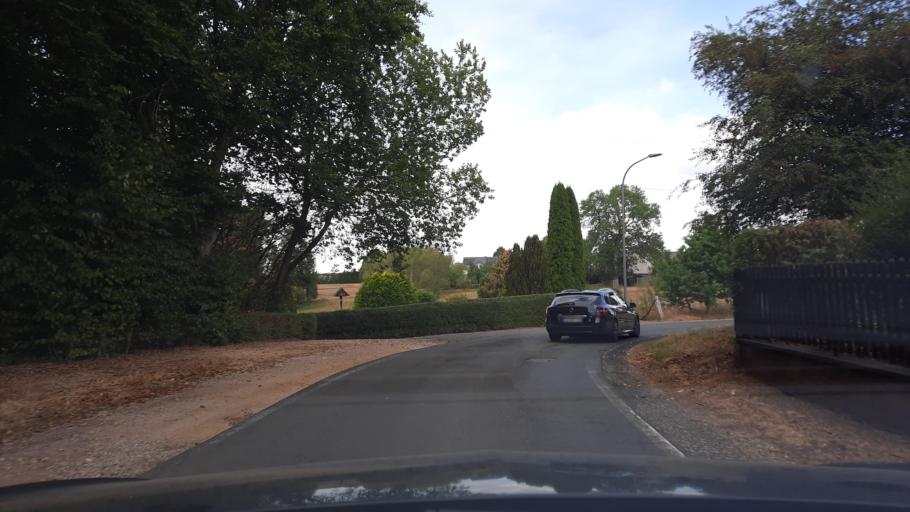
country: DE
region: Rheinland-Pfalz
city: Watzerath
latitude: 50.2027
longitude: 6.3679
